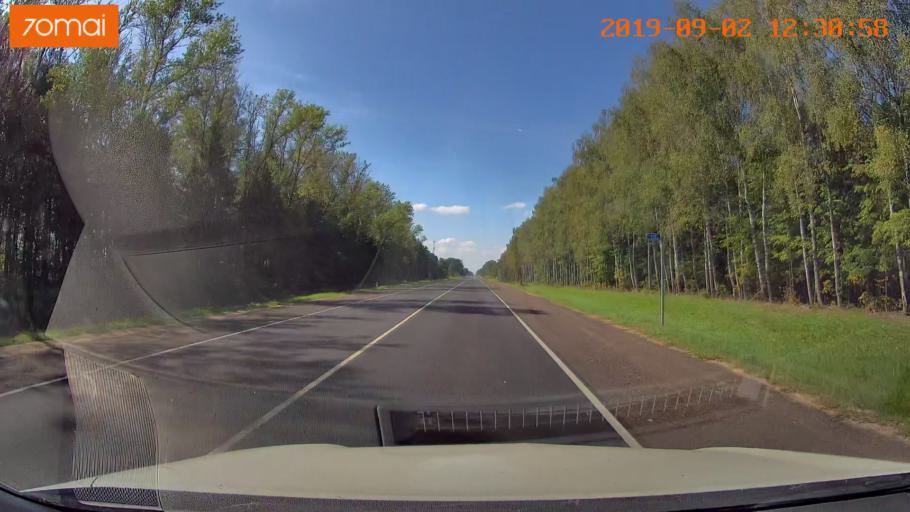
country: RU
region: Smolensk
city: Shumyachi
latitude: 53.8280
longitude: 32.4613
